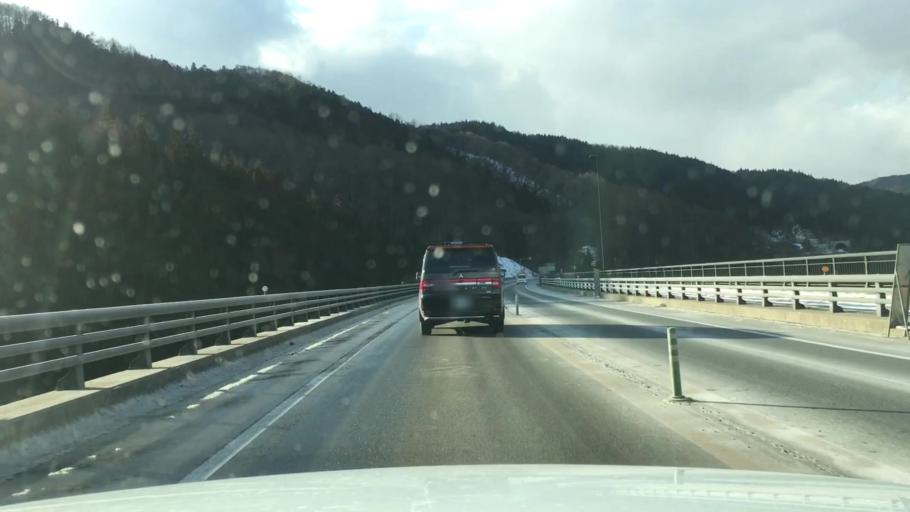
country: JP
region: Iwate
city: Morioka-shi
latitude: 39.6671
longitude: 141.2406
